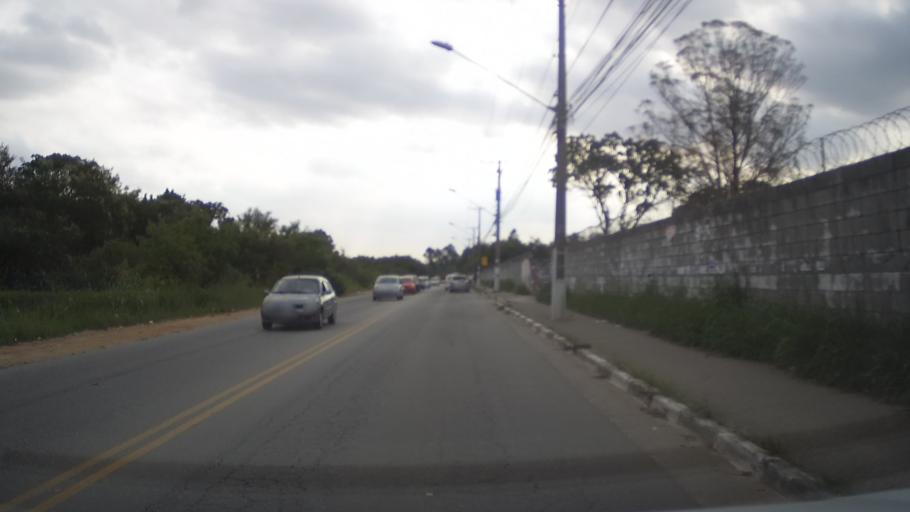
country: BR
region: Sao Paulo
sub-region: Guarulhos
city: Guarulhos
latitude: -23.4199
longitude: -46.4848
